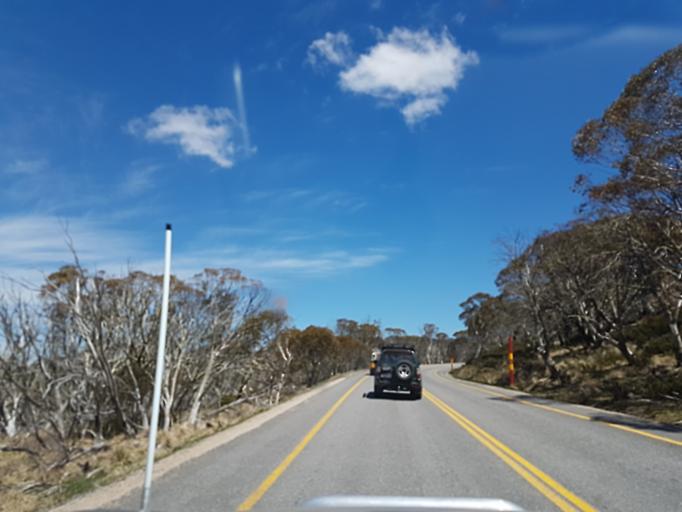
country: AU
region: Victoria
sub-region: Alpine
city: Mount Beauty
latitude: -37.0214
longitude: 147.2274
